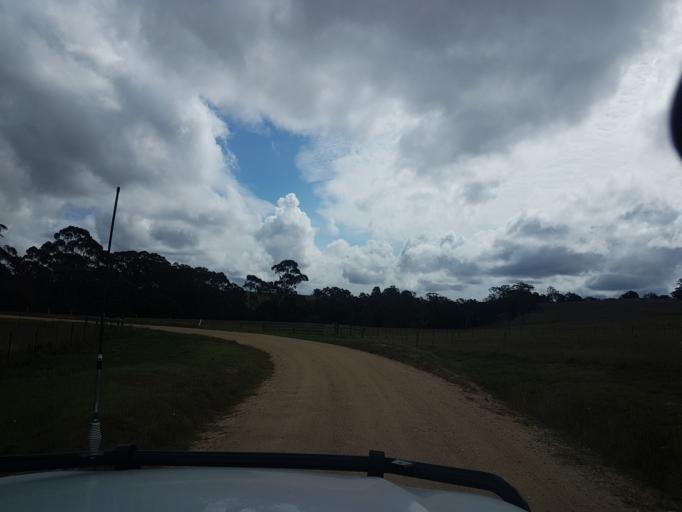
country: AU
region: Victoria
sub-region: East Gippsland
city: Bairnsdale
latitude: -37.7835
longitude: 147.5497
